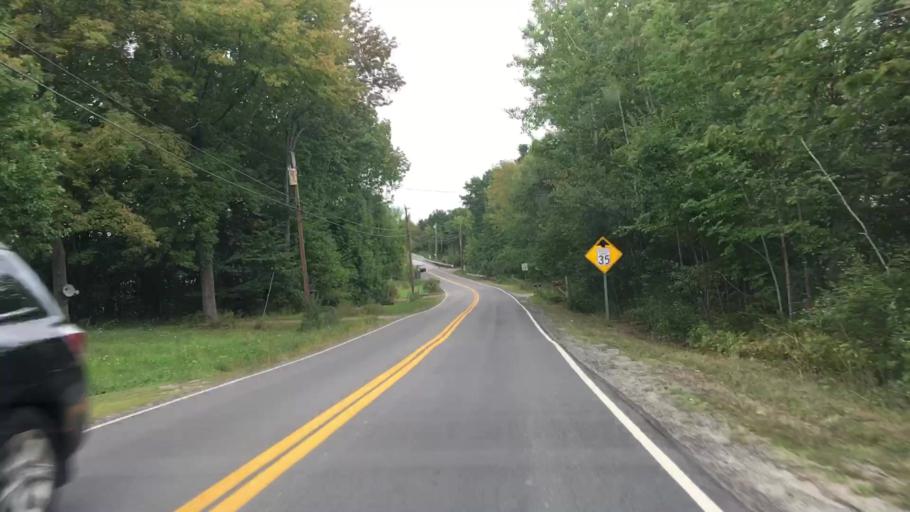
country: US
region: Maine
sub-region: Kennebec County
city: Hallowell
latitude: 44.2640
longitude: -69.8102
